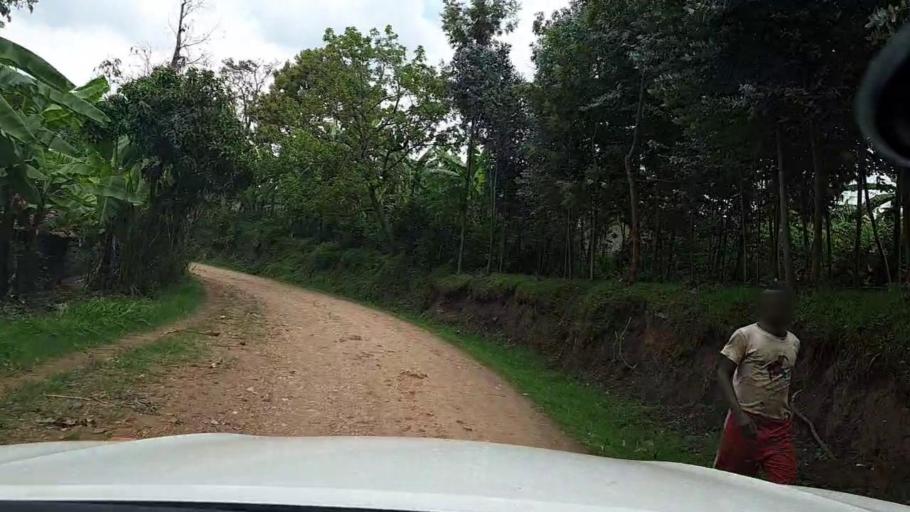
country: RW
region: Western Province
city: Kibuye
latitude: -2.0754
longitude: 29.4236
